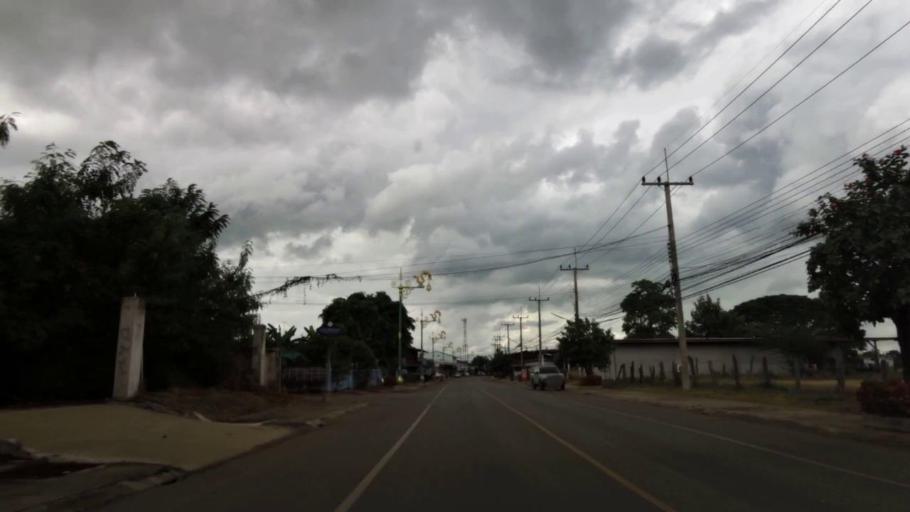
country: TH
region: Nakhon Sawan
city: Phai Sali
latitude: 15.5976
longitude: 100.6512
